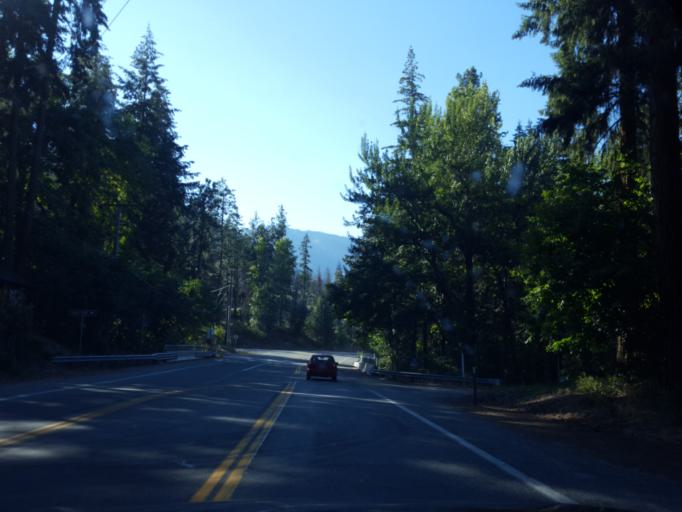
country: US
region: Washington
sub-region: Chelan County
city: Granite Falls
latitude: 47.8733
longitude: -120.1999
